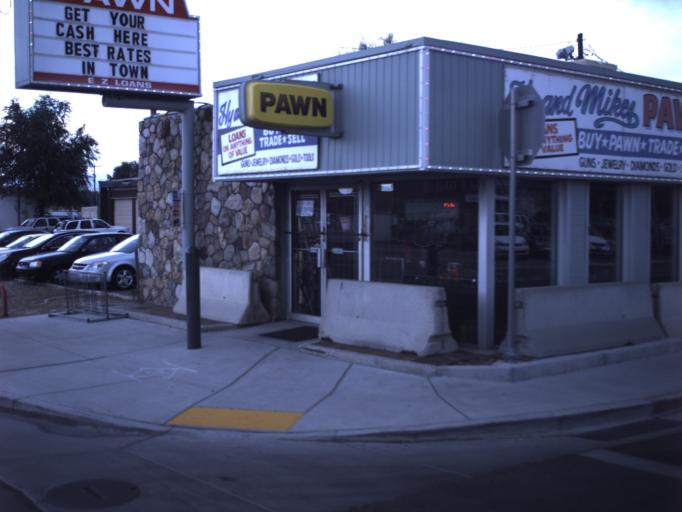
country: US
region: Utah
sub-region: Salt Lake County
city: Midvale
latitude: 40.6120
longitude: -111.8906
